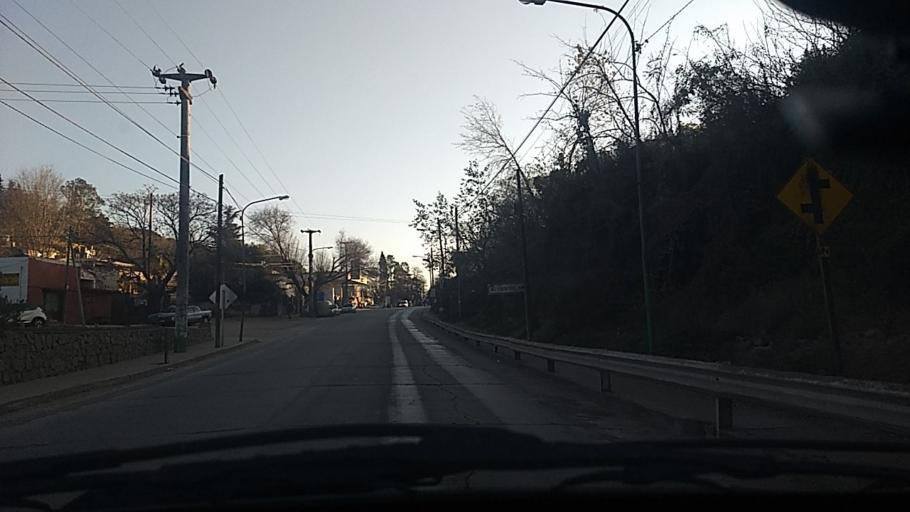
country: AR
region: Cordoba
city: Salsipuedes
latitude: -31.1385
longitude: -64.2968
